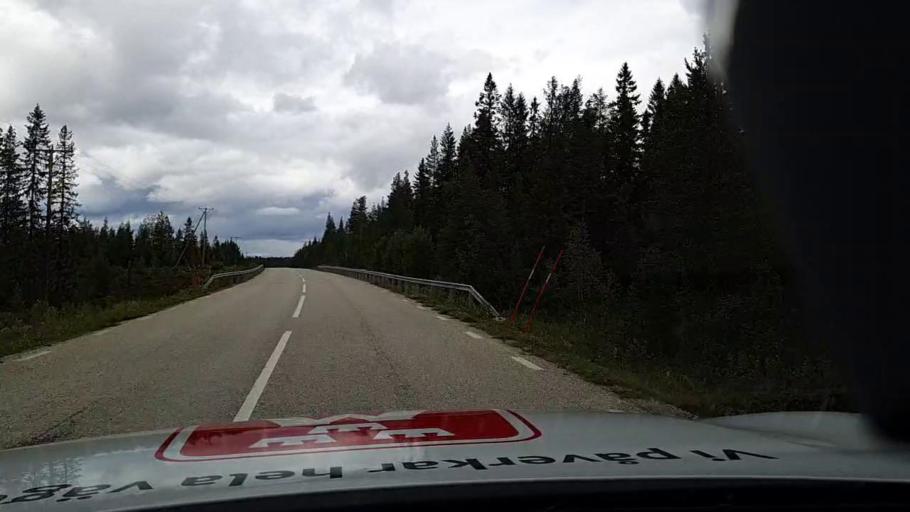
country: SE
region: Jaemtland
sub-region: Are Kommun
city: Jarpen
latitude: 62.7878
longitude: 13.6916
